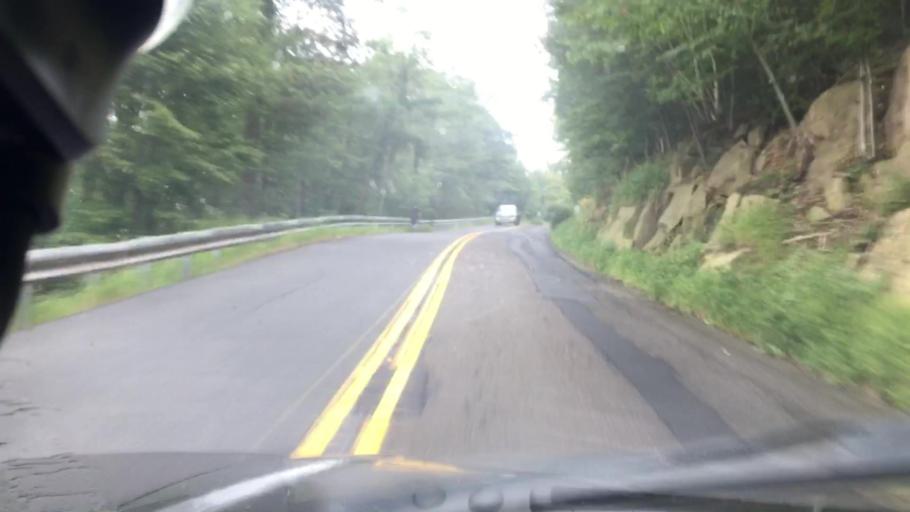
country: US
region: Pennsylvania
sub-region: Luzerne County
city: Harleigh
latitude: 41.0000
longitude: -75.9871
